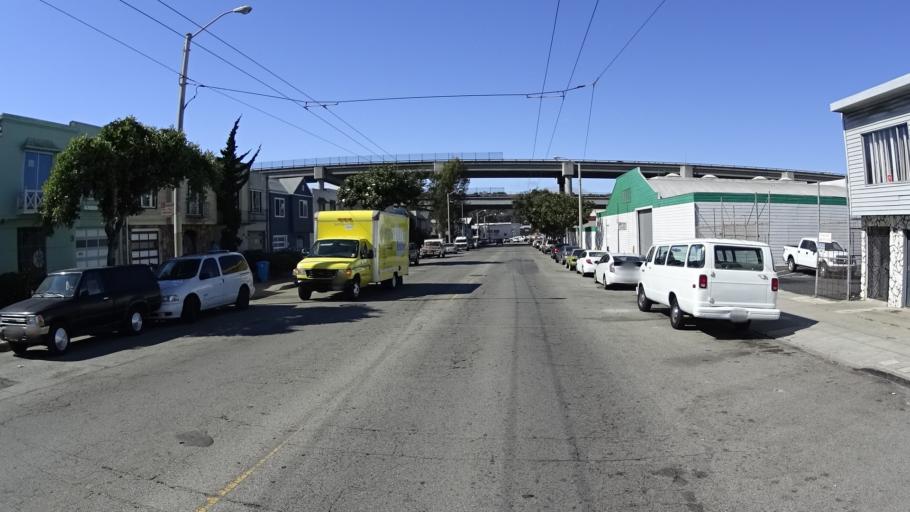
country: US
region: California
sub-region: San Francisco County
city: San Francisco
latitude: 37.7386
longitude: -122.3990
